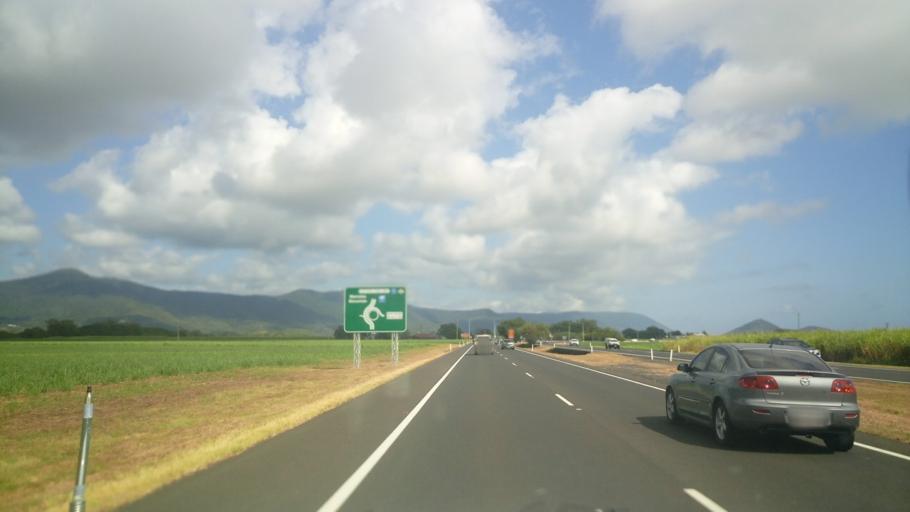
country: AU
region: Queensland
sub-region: Cairns
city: Redlynch
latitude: -16.8669
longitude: 145.7337
